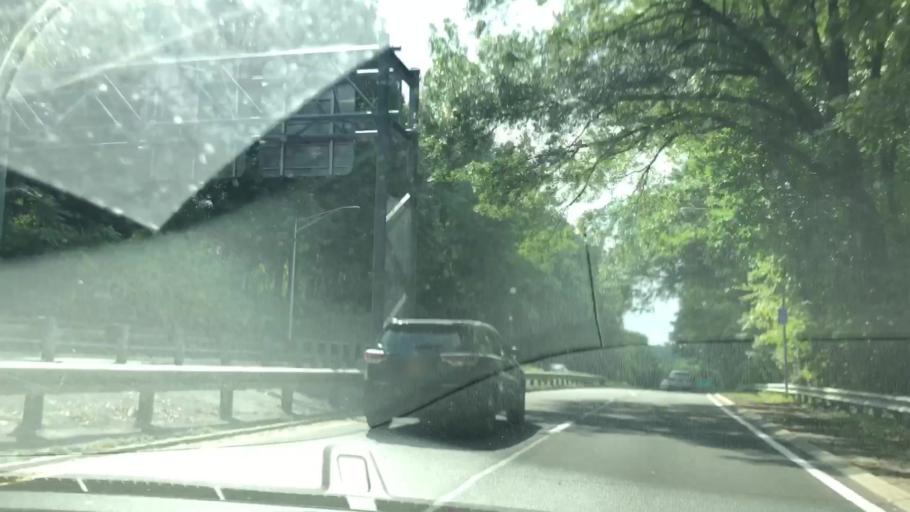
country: US
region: New York
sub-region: Westchester County
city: Yonkers
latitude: 40.8949
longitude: -73.8851
